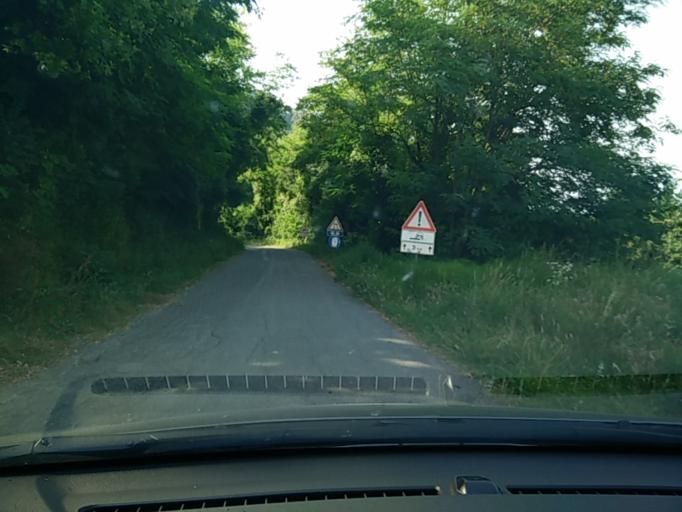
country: IT
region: Lombardy
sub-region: Provincia di Pavia
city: Susella
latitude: 44.9189
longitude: 9.1006
